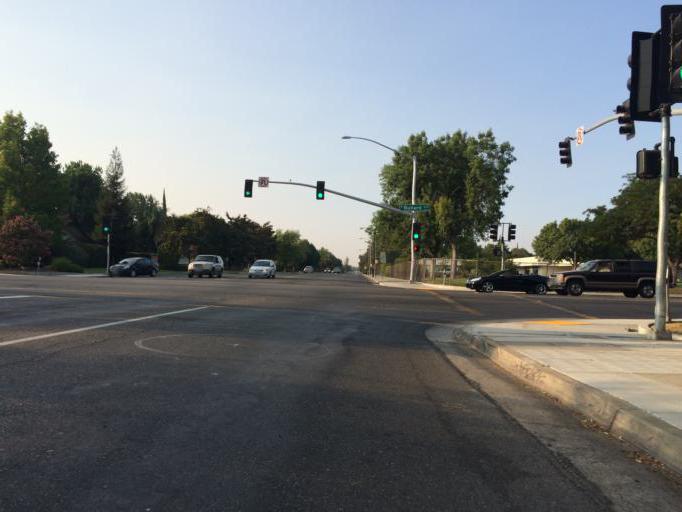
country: US
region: California
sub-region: Fresno County
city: Fresno
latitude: 36.8225
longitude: -119.8173
